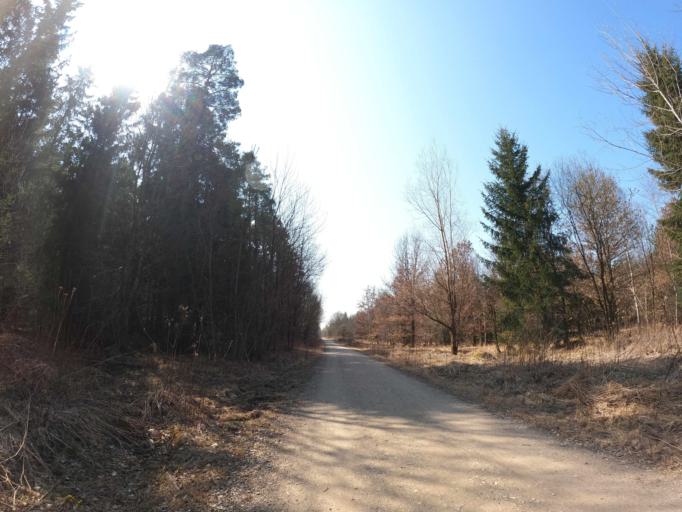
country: DE
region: Bavaria
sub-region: Upper Bavaria
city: Neuried
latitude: 48.0600
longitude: 11.4608
